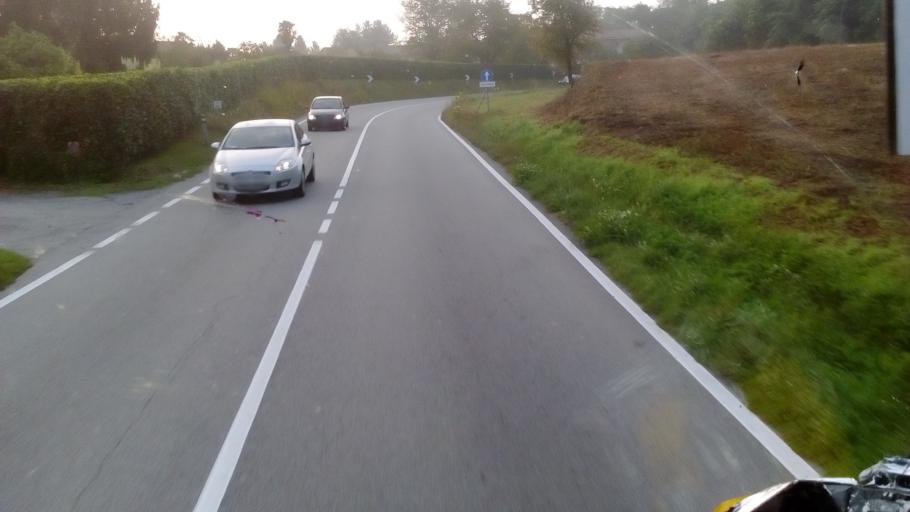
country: IT
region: Piedmont
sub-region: Provincia di Novara
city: Borgo Ticino
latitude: 45.6882
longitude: 8.6087
